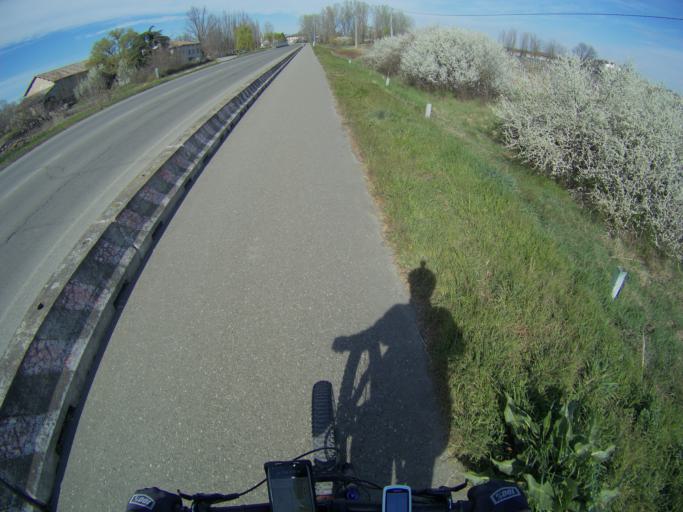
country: IT
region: Emilia-Romagna
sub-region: Provincia di Reggio Emilia
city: Massenzatico
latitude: 44.7200
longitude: 10.6946
